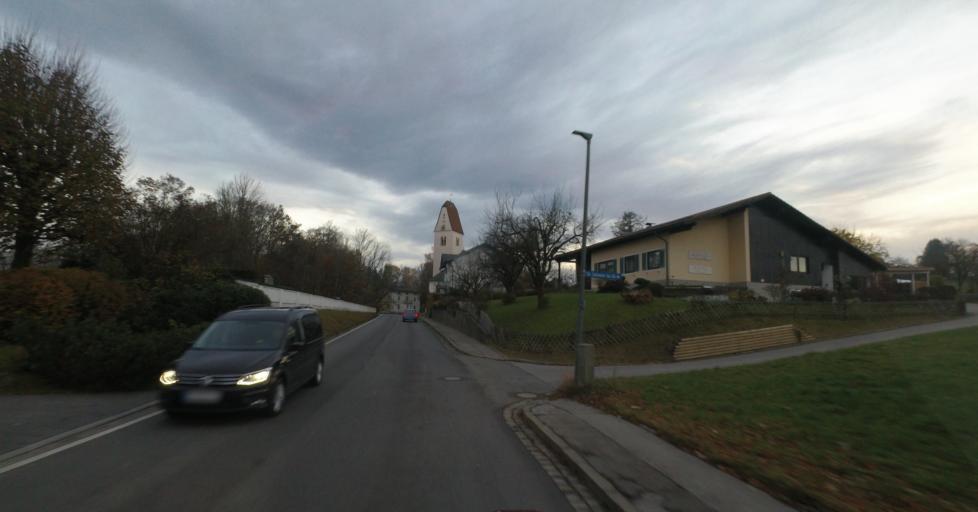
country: DE
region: Bavaria
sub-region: Upper Bavaria
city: Prien am Chiemsee
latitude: 47.8546
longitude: 12.3325
